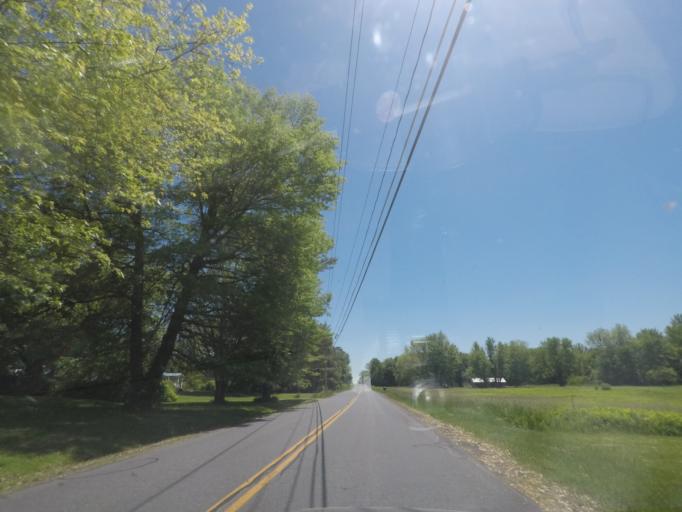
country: US
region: New York
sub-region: Saratoga County
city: Mechanicville
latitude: 42.9390
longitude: -73.6967
